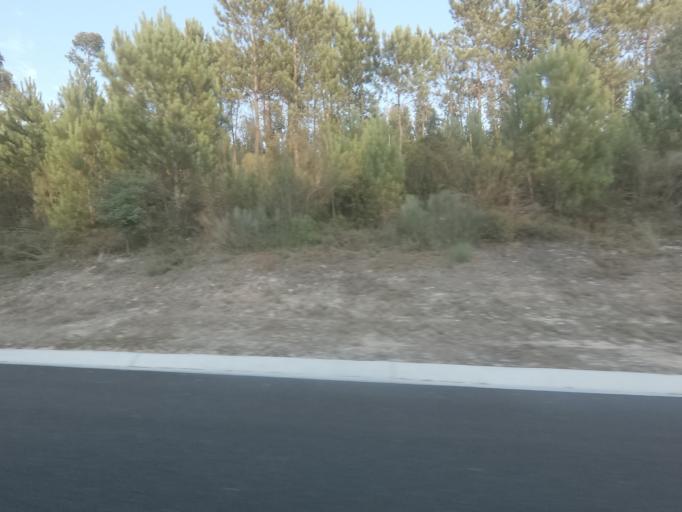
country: PT
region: Leiria
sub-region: Leiria
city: Caranguejeira
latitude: 39.7818
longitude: -8.7375
